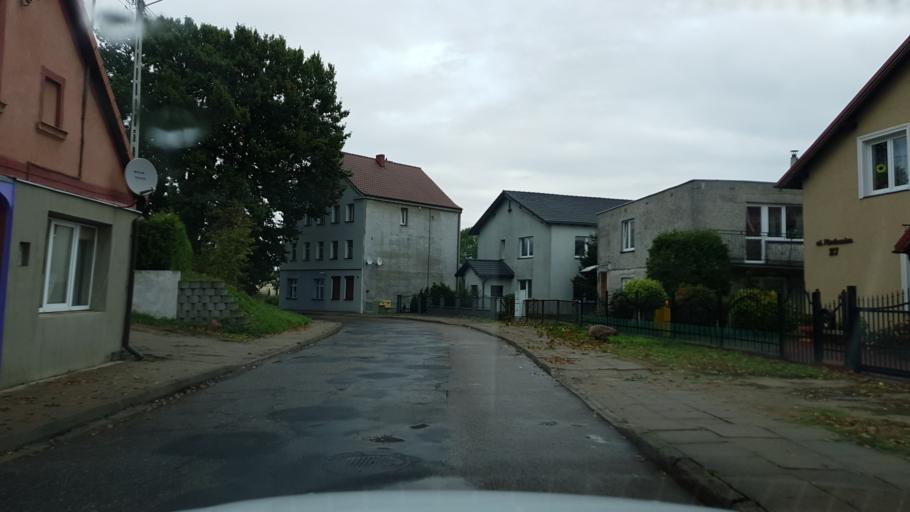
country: PL
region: West Pomeranian Voivodeship
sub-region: Powiat kamienski
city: Wolin
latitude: 53.8363
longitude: 14.6139
